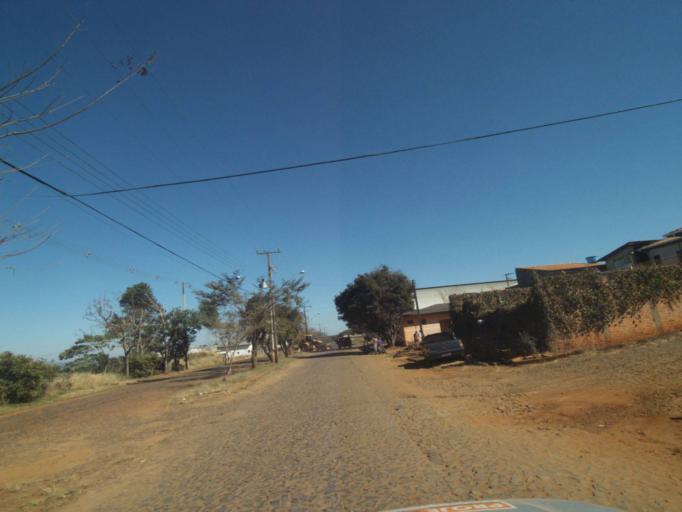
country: BR
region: Parana
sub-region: Reserva
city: Reserva
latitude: -24.6219
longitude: -50.6389
